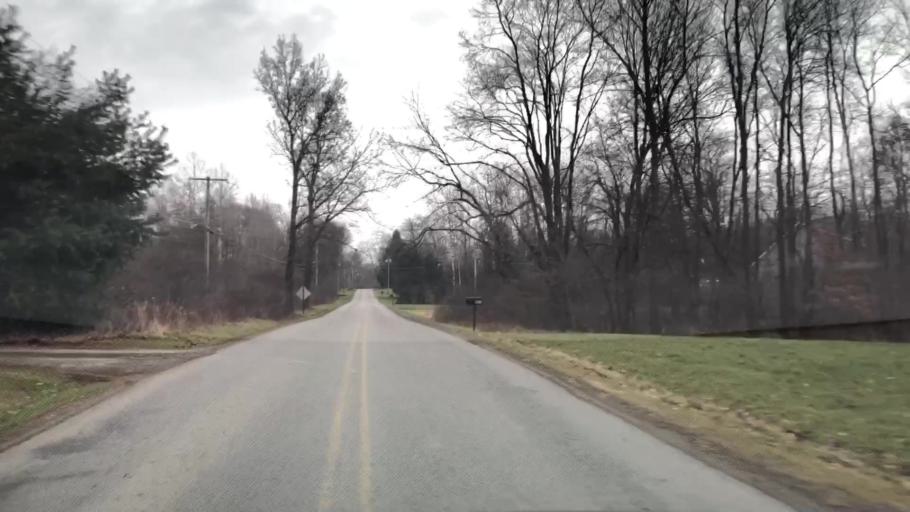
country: US
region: Pennsylvania
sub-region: Mercer County
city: Grove City
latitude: 41.1293
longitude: -80.0958
